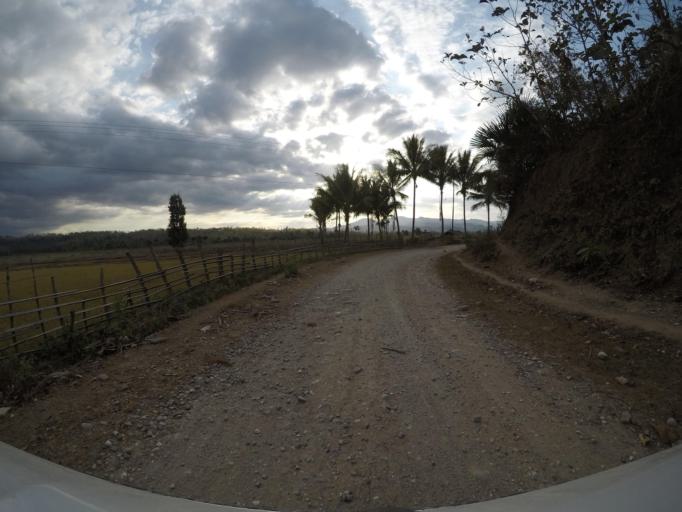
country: TL
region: Bobonaro
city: Maliana
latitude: -8.8905
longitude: 125.2091
